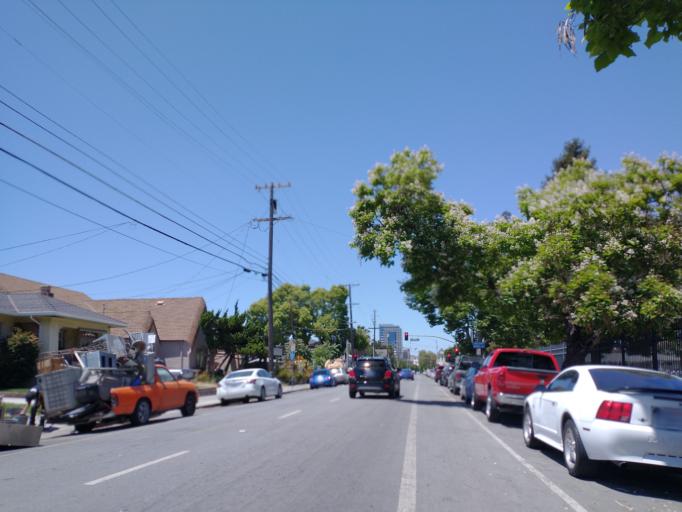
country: US
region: California
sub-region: Santa Clara County
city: San Jose
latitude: 37.3201
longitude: -121.8831
